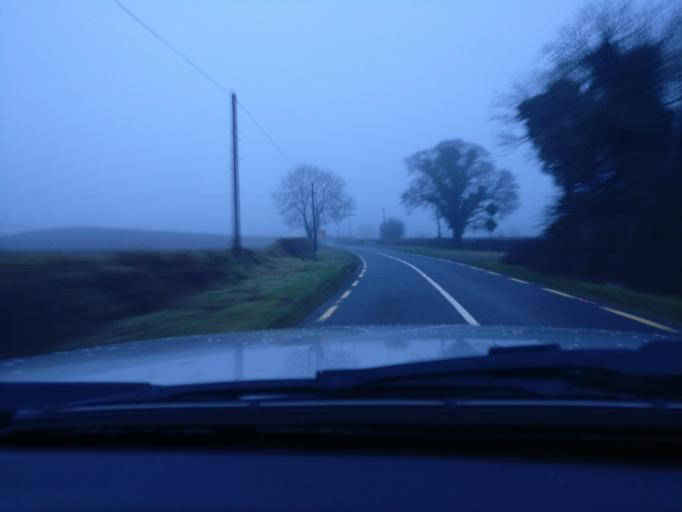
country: IE
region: Leinster
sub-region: An Mhi
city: Ballivor
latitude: 53.6085
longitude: -7.0092
